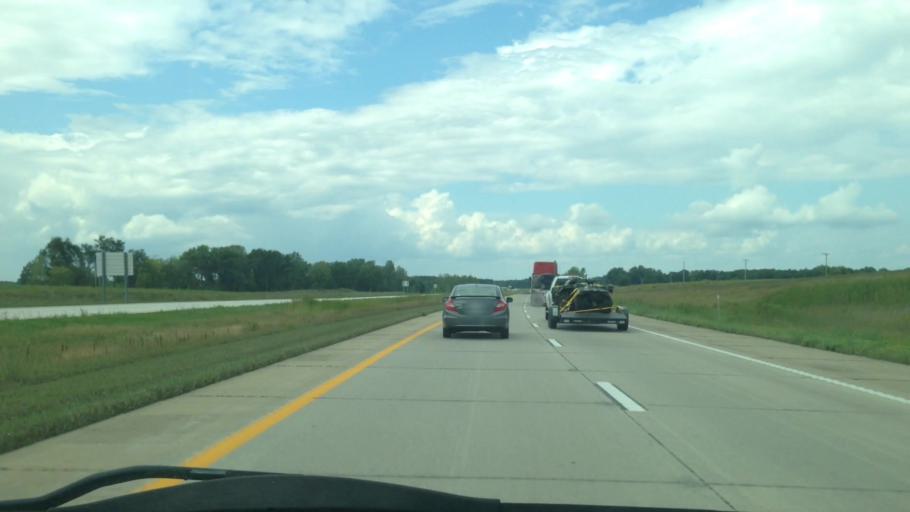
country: US
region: Missouri
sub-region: Pike County
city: Bowling Green
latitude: 39.3732
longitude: -91.2180
